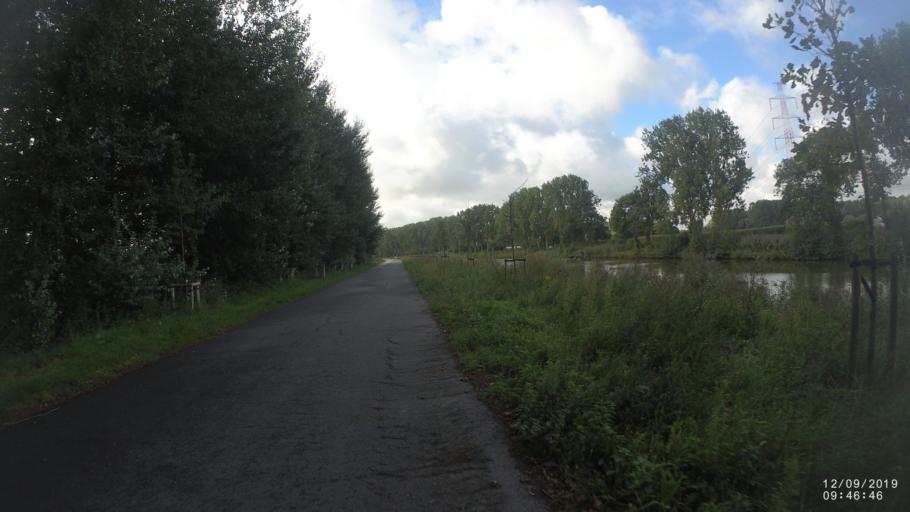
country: BE
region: Flanders
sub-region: Provincie Oost-Vlaanderen
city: Zomergem
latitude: 51.0832
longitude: 3.5635
